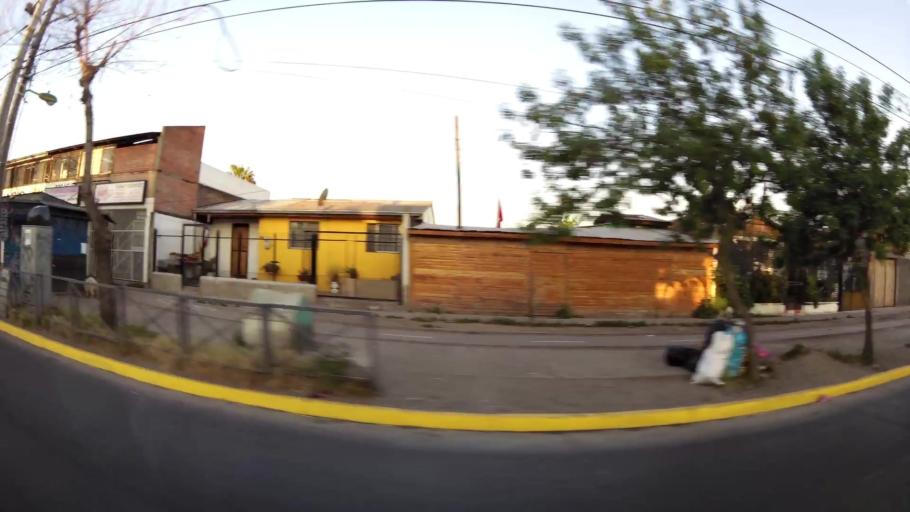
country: CL
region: Santiago Metropolitan
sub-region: Provincia de Maipo
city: San Bernardo
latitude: -33.5667
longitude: -70.6722
